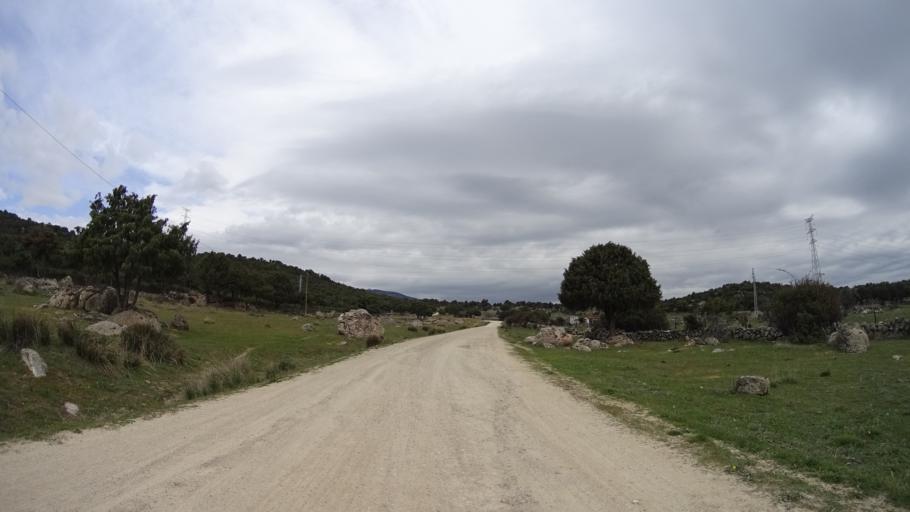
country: ES
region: Madrid
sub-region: Provincia de Madrid
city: Hoyo de Manzanares
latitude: 40.6117
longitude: -3.8782
